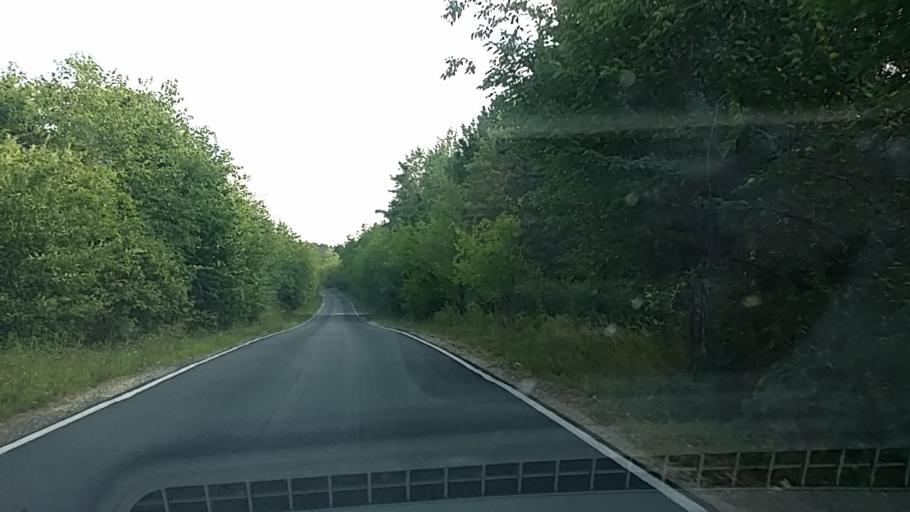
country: HU
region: Gyor-Moson-Sopron
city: Fertorakos
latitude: 47.7336
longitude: 16.6201
